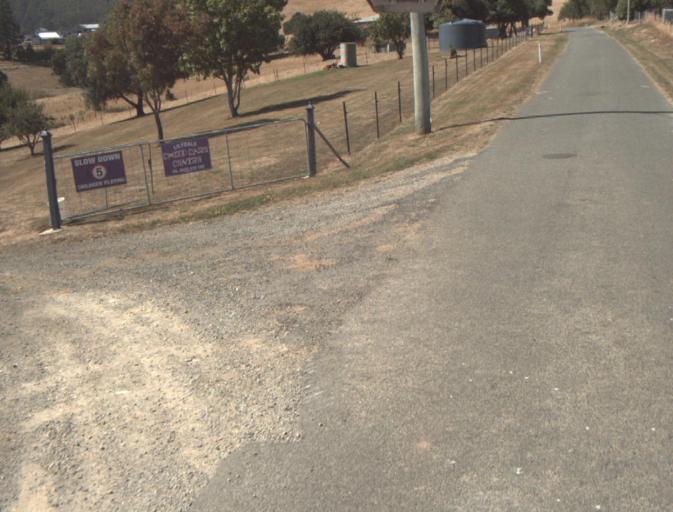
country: AU
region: Tasmania
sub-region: Launceston
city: Mayfield
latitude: -41.2344
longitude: 147.2556
